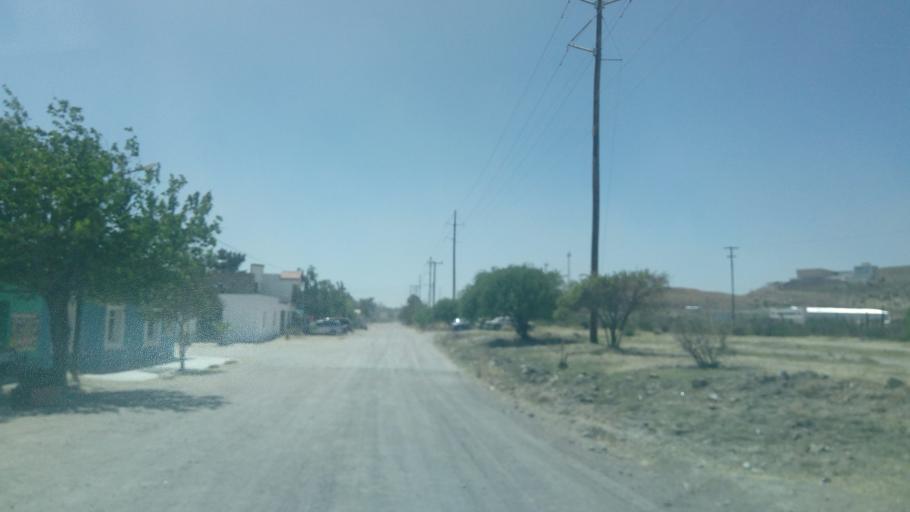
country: MX
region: Durango
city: Victoria de Durango
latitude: 24.0756
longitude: -104.6580
